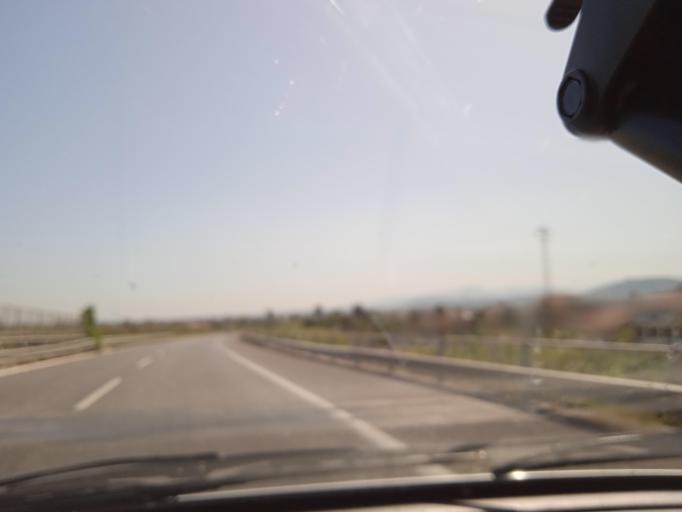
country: IT
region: Sicily
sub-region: Messina
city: Barcellona Pozzo di Gotto
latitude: 38.1628
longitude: 15.2007
